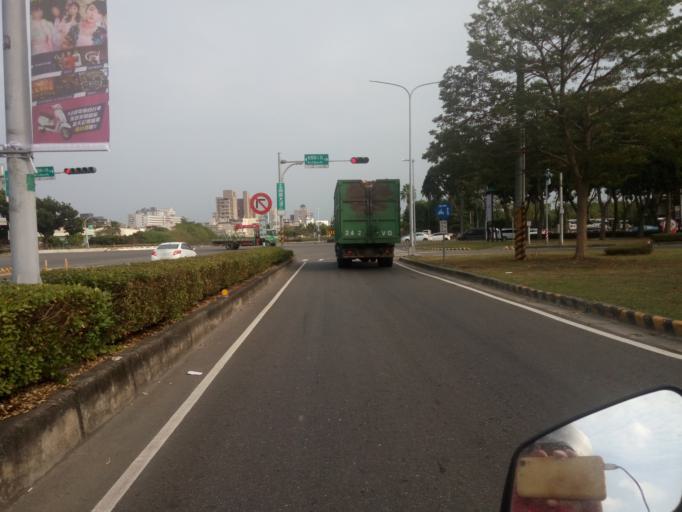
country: TW
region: Taiwan
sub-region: Chiayi
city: Jiayi Shi
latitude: 23.4819
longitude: 120.4200
